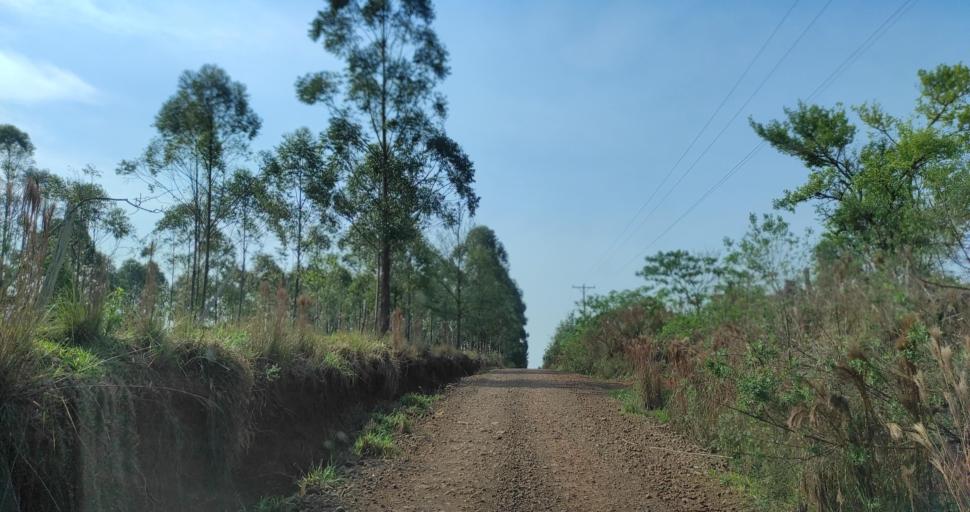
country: AR
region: Misiones
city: Capiovi
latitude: -26.8863
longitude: -55.0486
